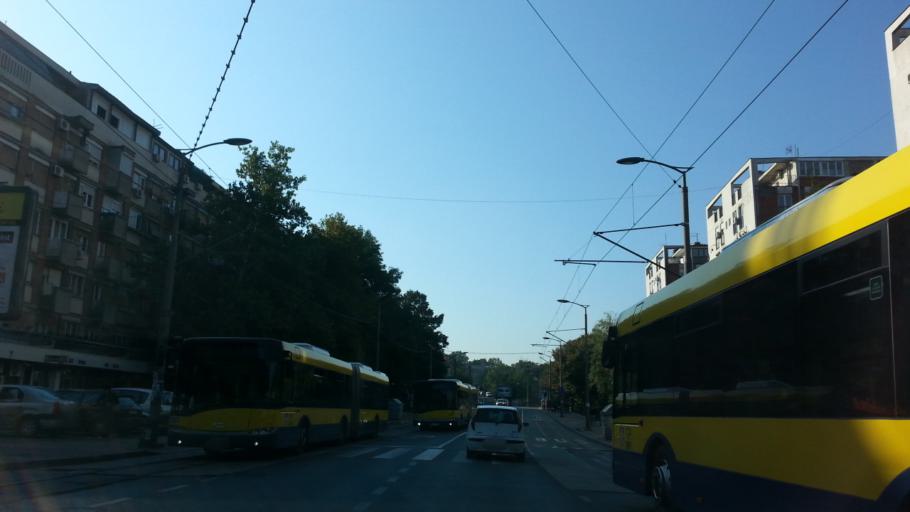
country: RS
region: Central Serbia
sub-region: Belgrade
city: Cukarica
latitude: 44.7723
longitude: 20.4142
